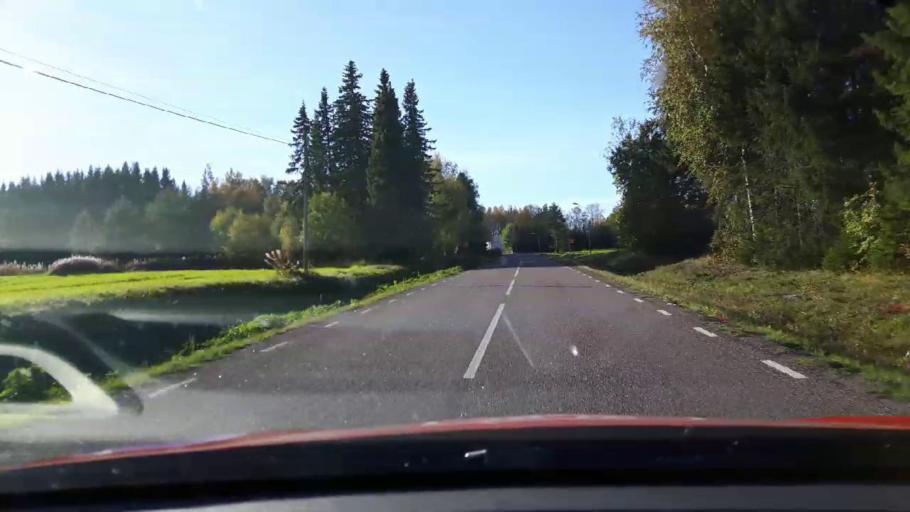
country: SE
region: Jaemtland
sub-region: Stroemsunds Kommun
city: Stroemsund
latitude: 63.8439
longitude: 15.3463
